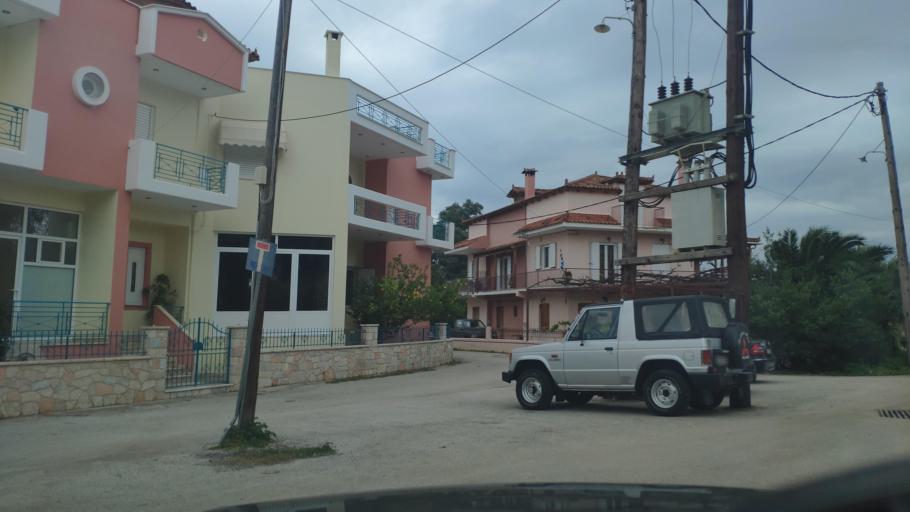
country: GR
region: Peloponnese
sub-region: Nomos Argolidos
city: Nea Kios
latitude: 37.5543
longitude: 22.7178
